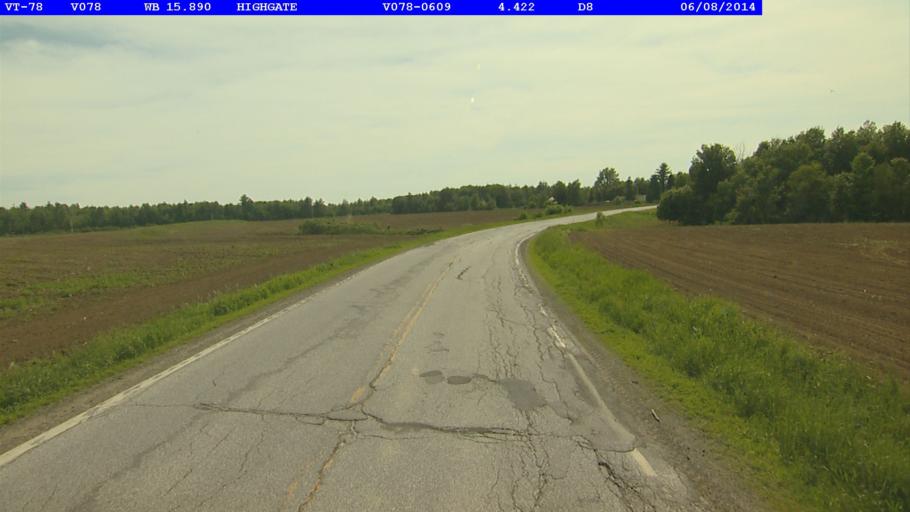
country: US
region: Vermont
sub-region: Franklin County
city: Swanton
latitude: 44.9455
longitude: -73.0197
